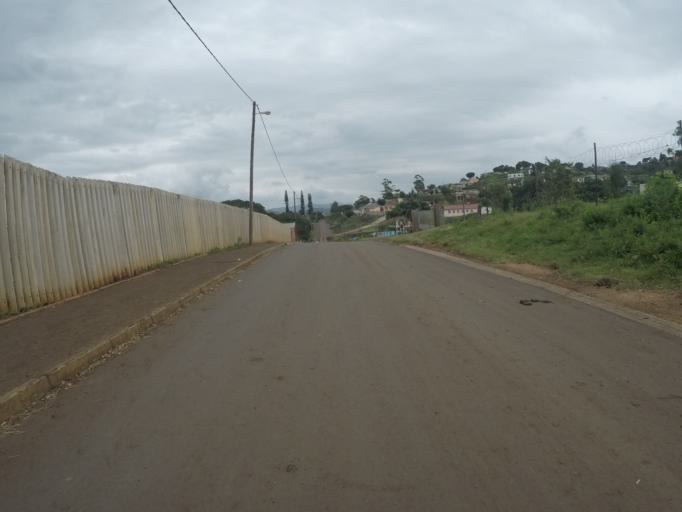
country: ZA
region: KwaZulu-Natal
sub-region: uThungulu District Municipality
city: Empangeni
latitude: -28.7710
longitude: 31.8590
